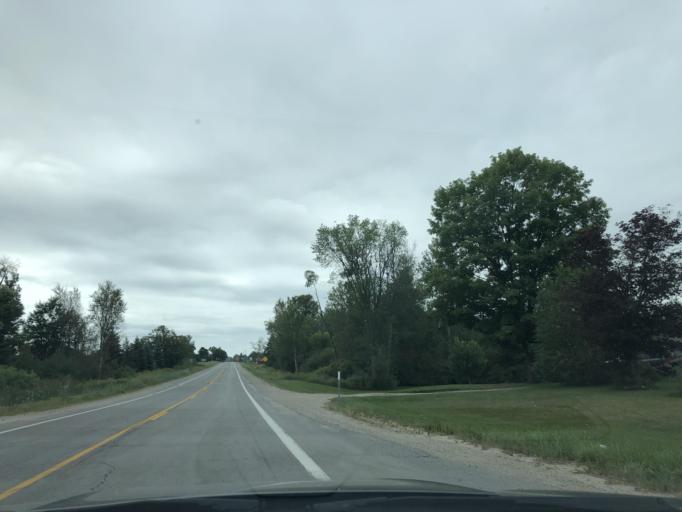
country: US
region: Michigan
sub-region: Missaukee County
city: Lake City
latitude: 44.2084
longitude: -85.2143
